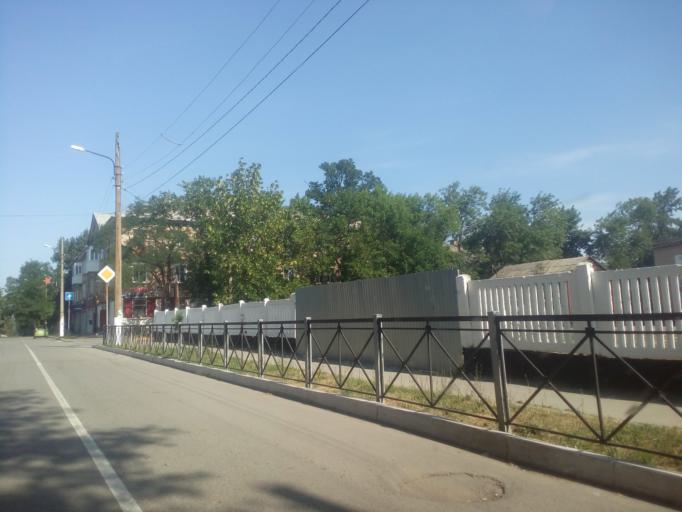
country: RU
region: Rostov
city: Sholokhovskiy
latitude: 48.2825
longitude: 41.0422
